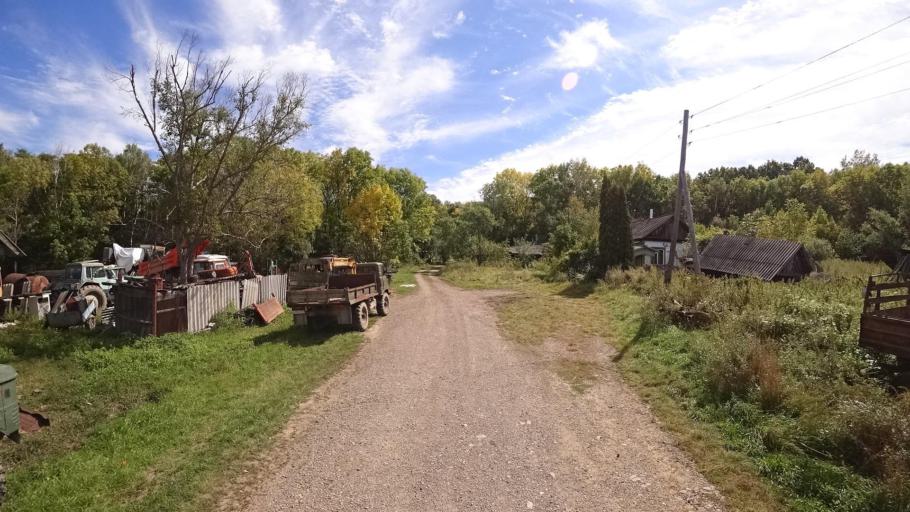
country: RU
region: Primorskiy
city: Yakovlevka
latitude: 44.6529
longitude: 133.7483
